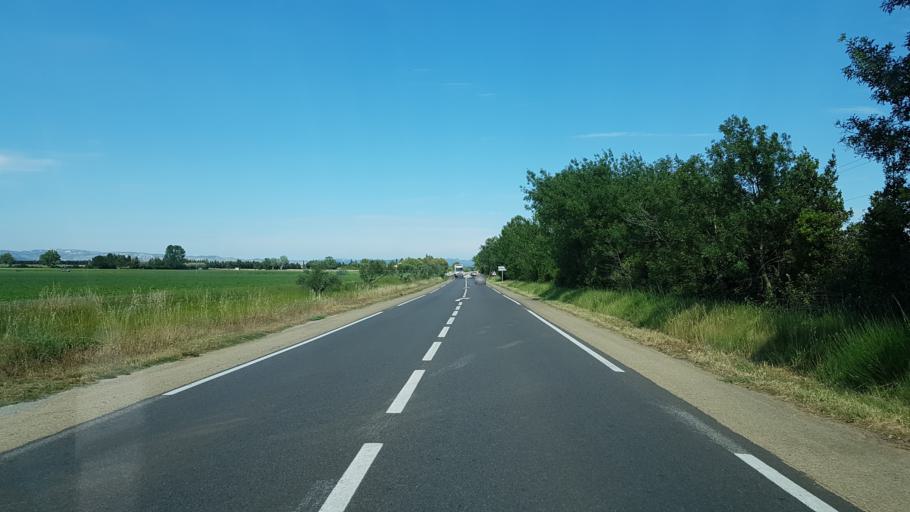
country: FR
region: Provence-Alpes-Cote d'Azur
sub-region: Departement des Bouches-du-Rhone
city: Fontvieille
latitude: 43.6654
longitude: 4.7216
